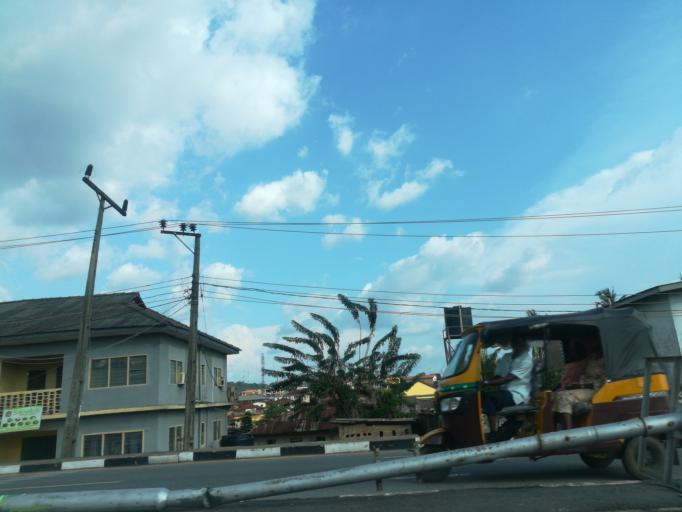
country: NG
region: Oyo
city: Ibadan
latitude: 7.3958
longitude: 3.8819
